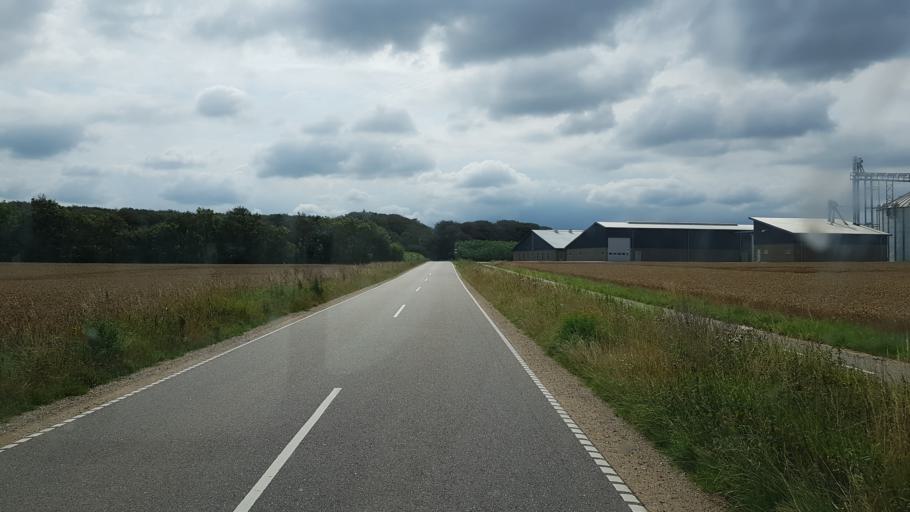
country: DK
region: South Denmark
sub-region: Varde Kommune
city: Varde
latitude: 55.7418
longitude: 8.4889
